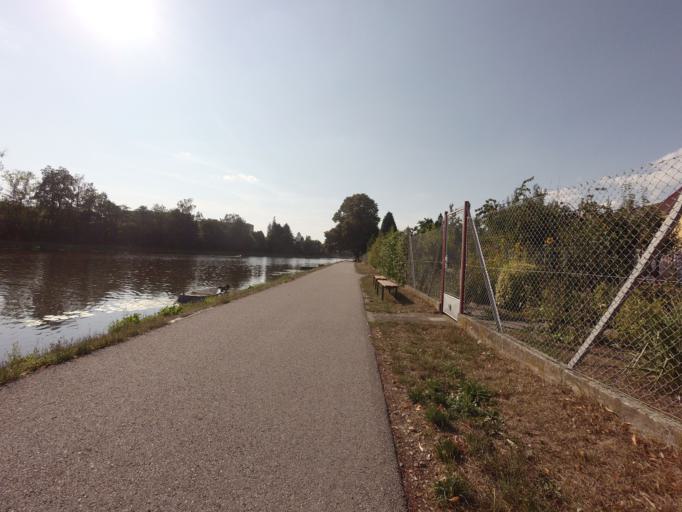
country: CZ
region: Jihocesky
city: Tyn nad Vltavou
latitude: 49.2177
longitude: 14.4309
